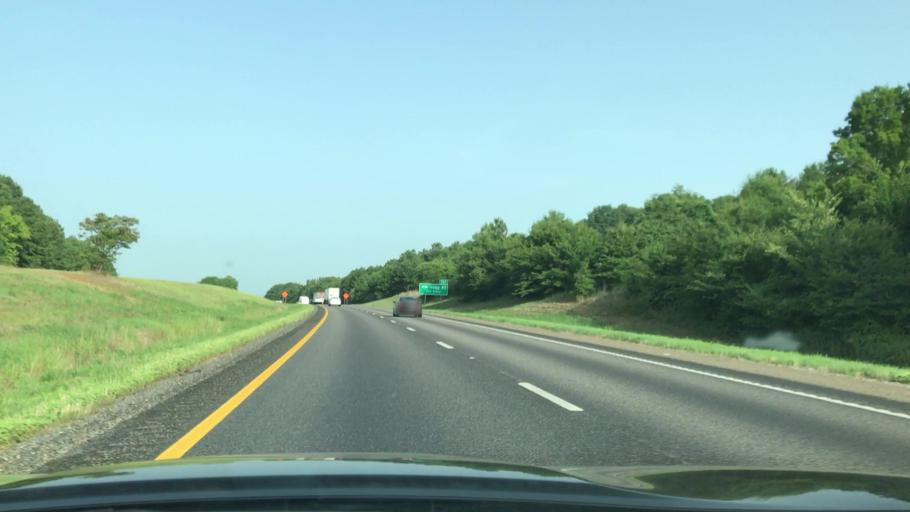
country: US
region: Texas
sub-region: Smith County
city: Lindale
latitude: 32.4686
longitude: -95.3449
